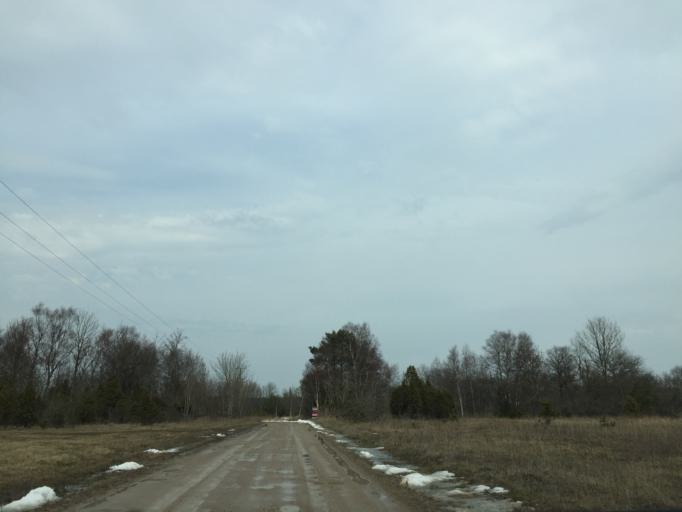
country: EE
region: Saare
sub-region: Kuressaare linn
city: Kuressaare
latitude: 58.4378
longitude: 22.1452
